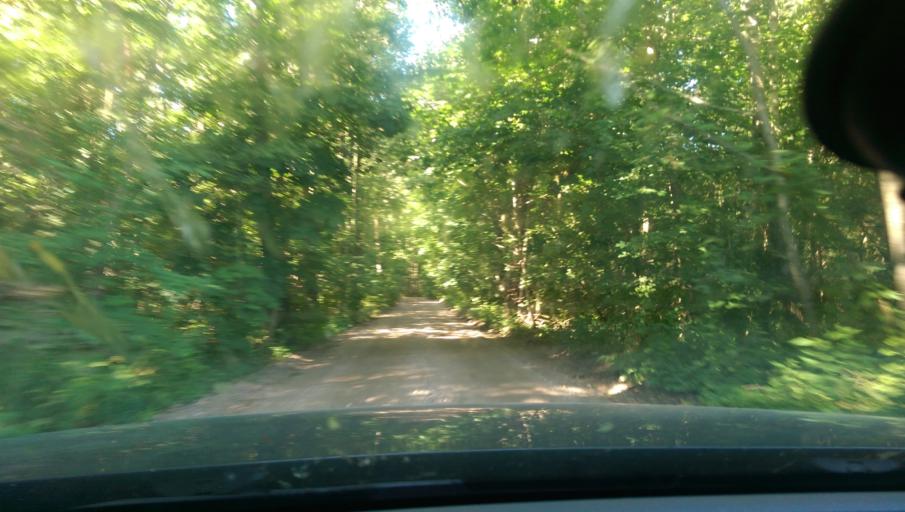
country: LT
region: Klaipedos apskritis
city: Gargzdai
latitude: 55.6525
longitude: 21.3319
